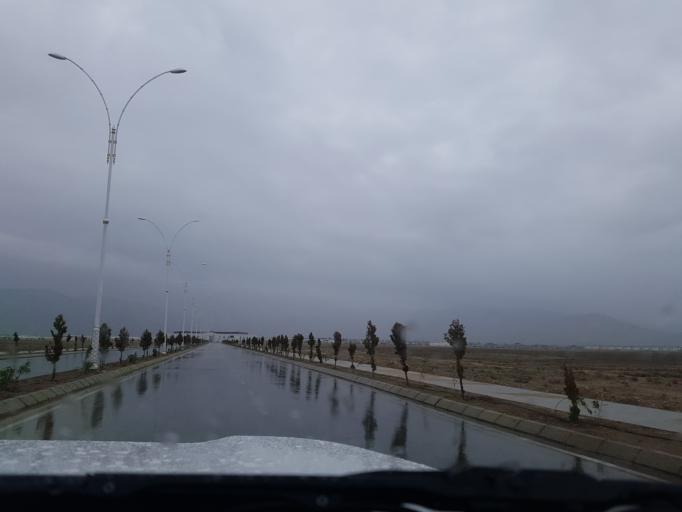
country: TM
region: Balkan
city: Balkanabat
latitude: 39.5558
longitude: 54.2941
